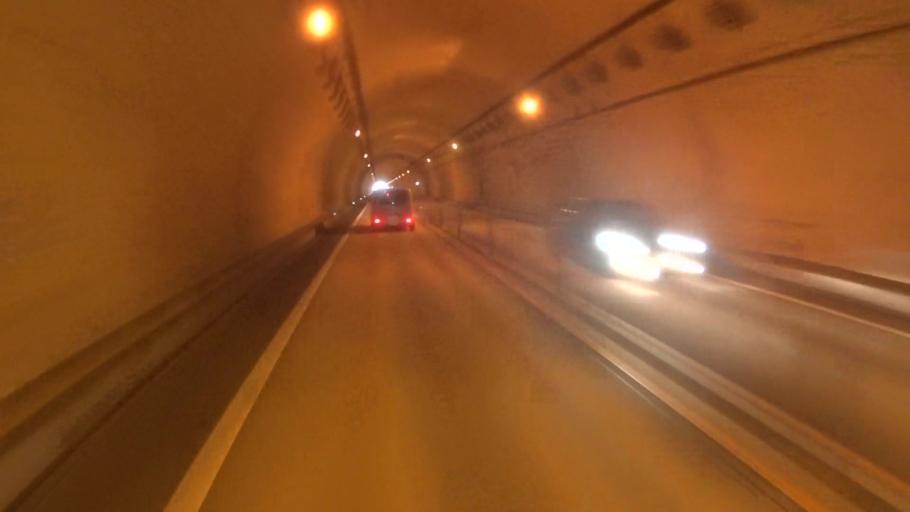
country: JP
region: Kyoto
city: Miyazu
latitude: 35.4567
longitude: 135.1773
